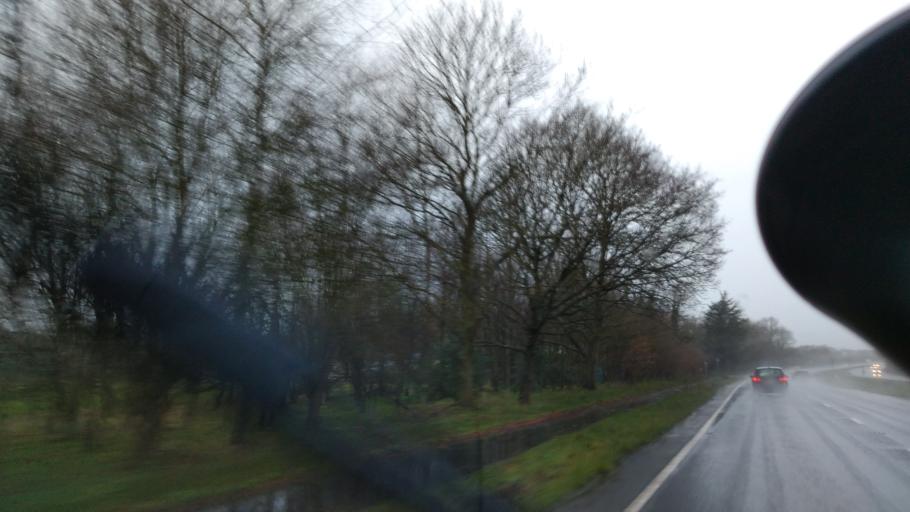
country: GB
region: England
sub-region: West Sussex
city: Rustington
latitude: 50.8413
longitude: -0.4934
